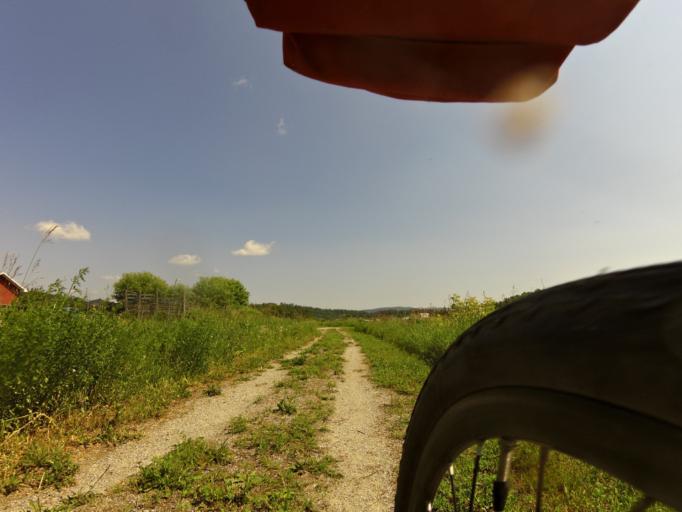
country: CA
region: Quebec
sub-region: Outaouais
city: Wakefield
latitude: 45.7956
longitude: -75.9452
